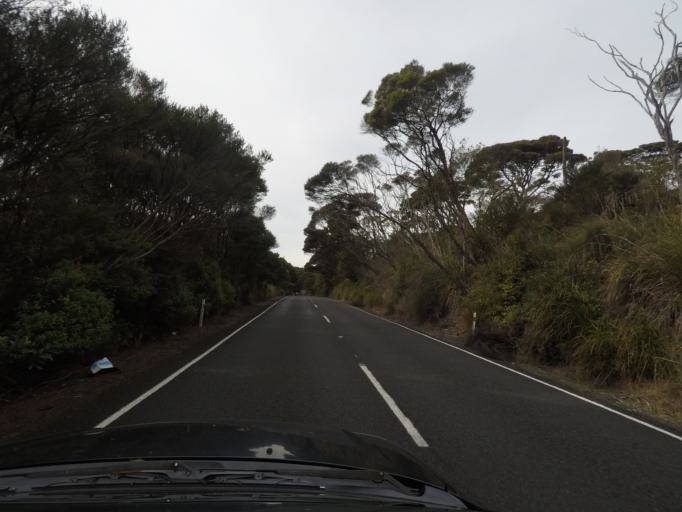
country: NZ
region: Auckland
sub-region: Auckland
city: Titirangi
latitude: -36.9342
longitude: 174.5650
